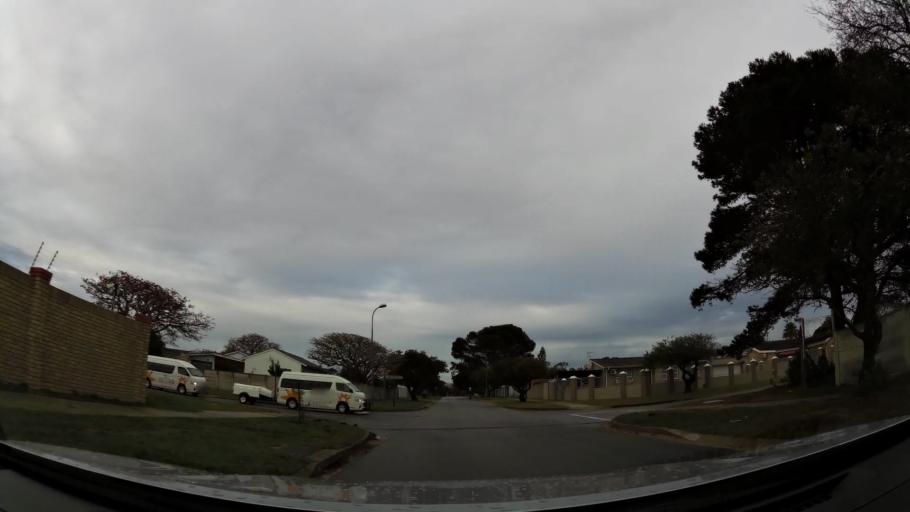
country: ZA
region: Eastern Cape
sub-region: Nelson Mandela Bay Metropolitan Municipality
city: Port Elizabeth
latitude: -33.9833
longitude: 25.5587
